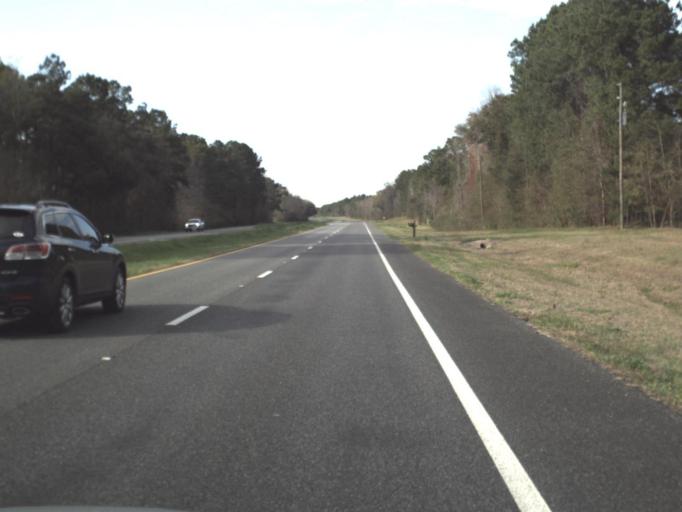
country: US
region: Florida
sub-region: Jefferson County
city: Monticello
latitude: 30.6284
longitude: -83.8727
